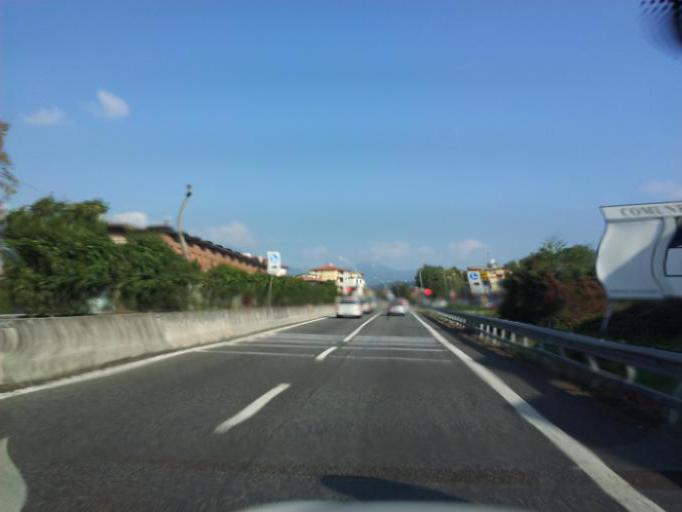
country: IT
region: Lombardy
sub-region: Provincia di Varese
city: Besozzo
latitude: 45.8401
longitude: 8.6679
